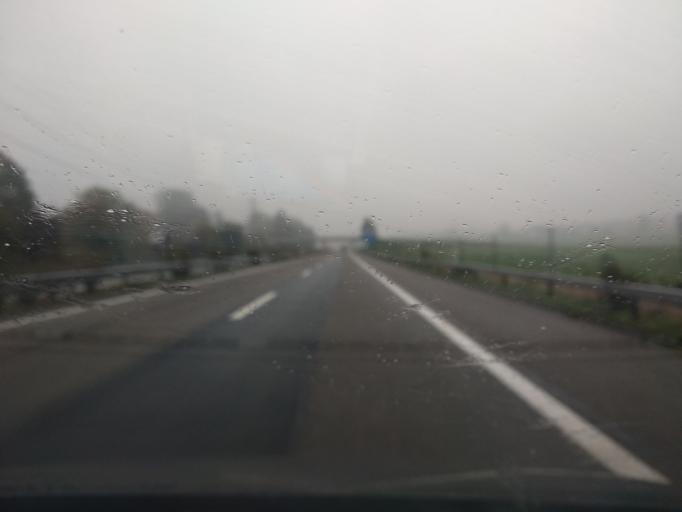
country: CH
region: Saint Gallen
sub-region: Wahlkreis Wil
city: Uzwil
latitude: 47.4544
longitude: 9.1338
